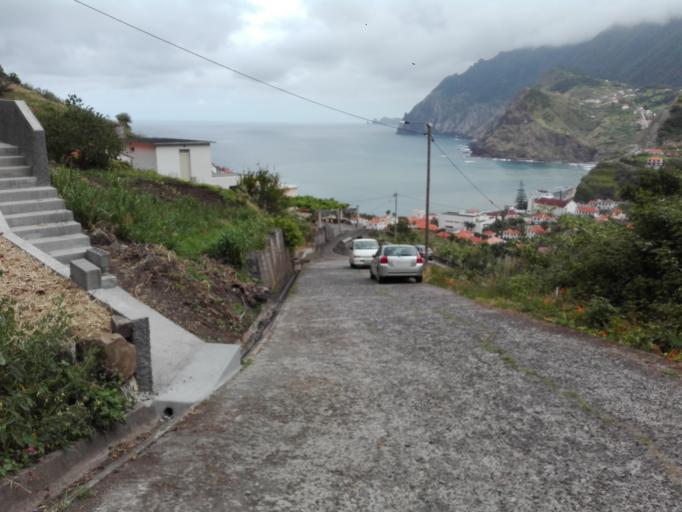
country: PT
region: Madeira
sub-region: Santana
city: Santana
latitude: 32.7744
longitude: -16.8332
